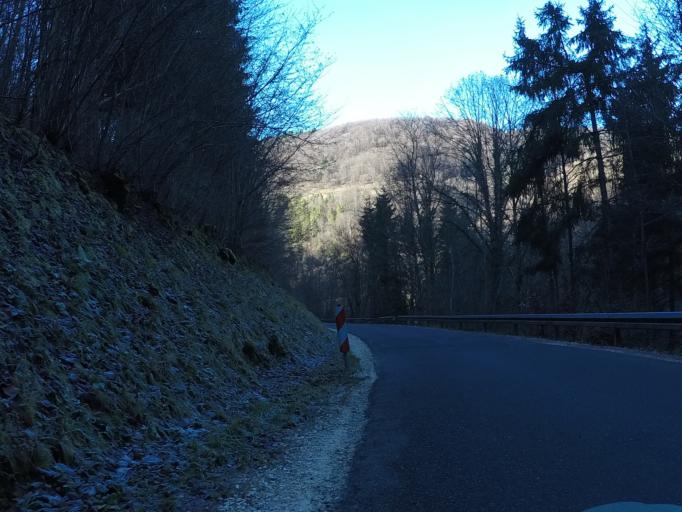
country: DE
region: Baden-Wuerttemberg
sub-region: Tuebingen Region
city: Eningen unter Achalm
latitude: 48.4474
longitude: 9.2860
